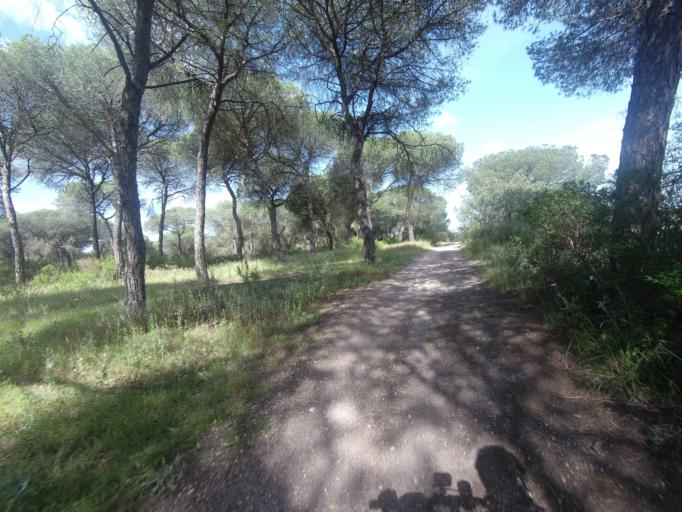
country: ES
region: Andalusia
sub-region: Provincia de Huelva
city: Aljaraque
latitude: 37.2344
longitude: -7.0413
